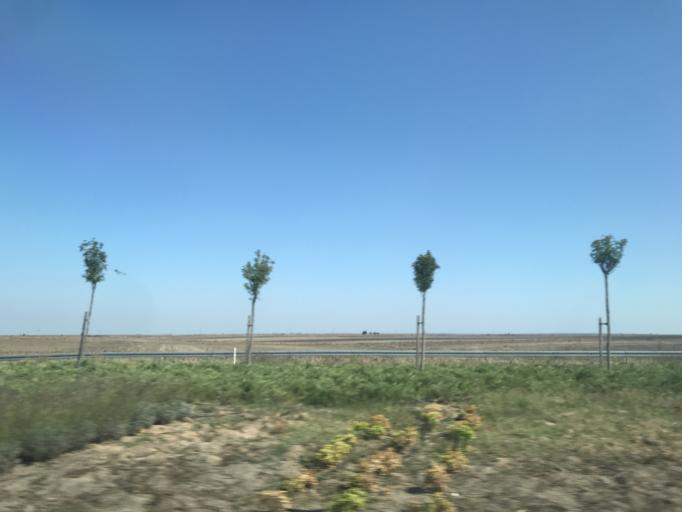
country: TR
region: Tekirdag
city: Muratli
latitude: 41.1954
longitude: 27.5385
